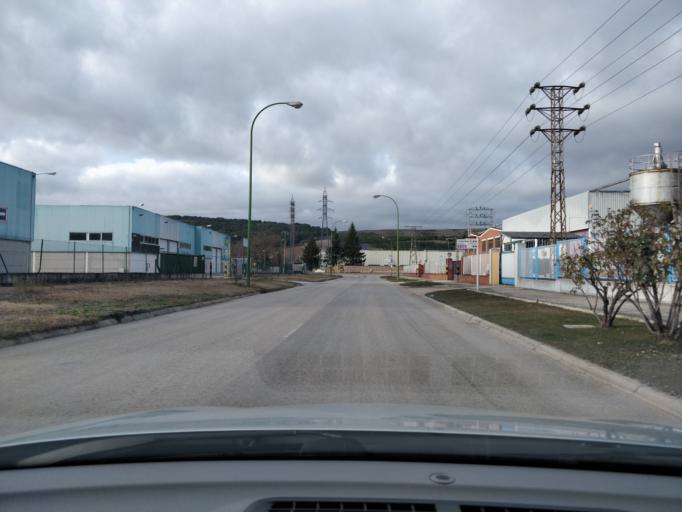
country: ES
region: Castille and Leon
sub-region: Provincia de Burgos
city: Villalbilla de Burgos
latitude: 42.3632
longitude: -3.7577
